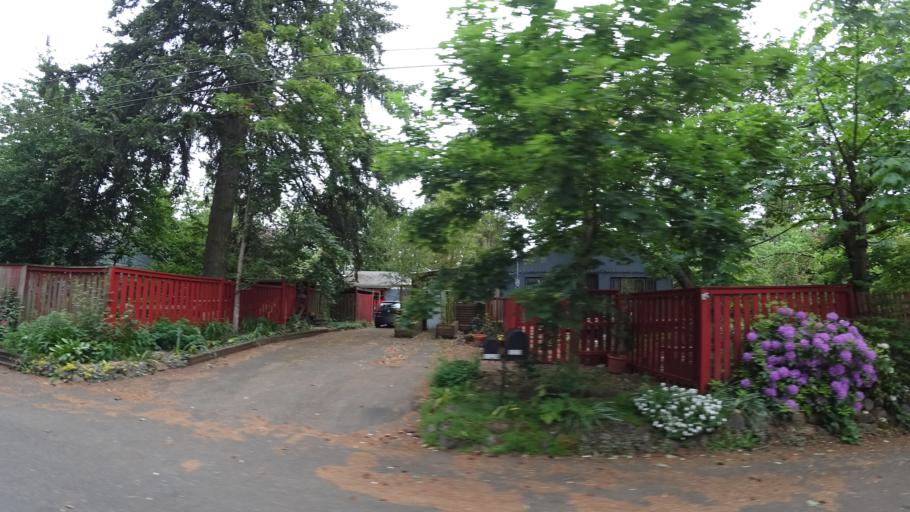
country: US
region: Oregon
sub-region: Multnomah County
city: Lents
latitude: 45.5137
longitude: -122.5452
